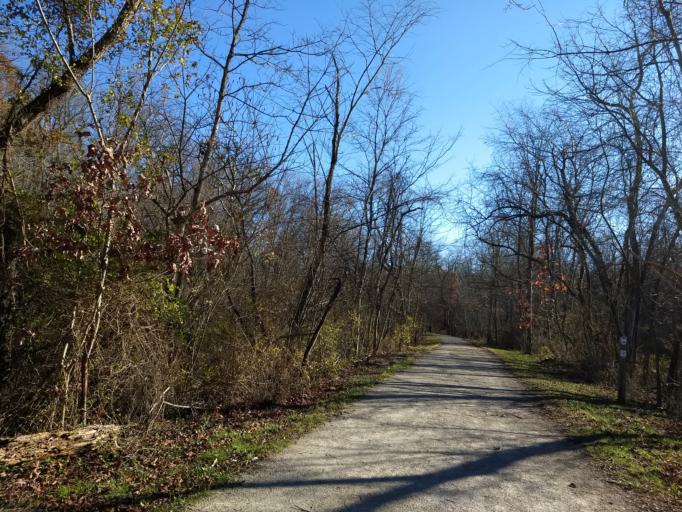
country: US
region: Pennsylvania
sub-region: Allegheny County
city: South Park Township
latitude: 40.2840
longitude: -79.9885
